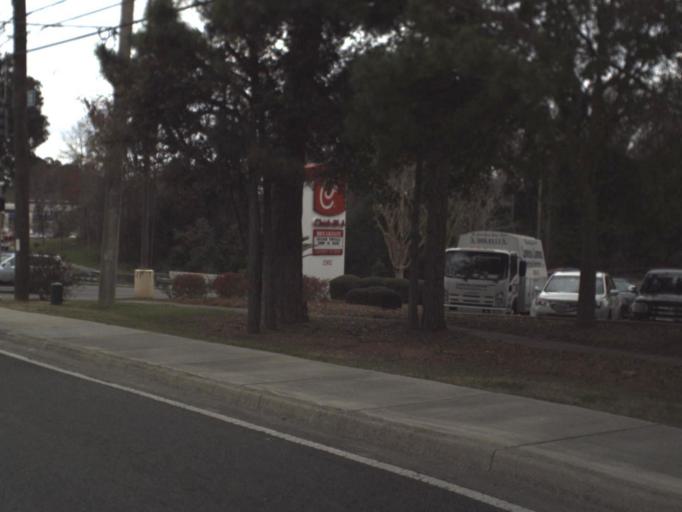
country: US
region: Florida
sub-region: Leon County
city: Tallahassee
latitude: 30.4299
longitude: -84.2432
